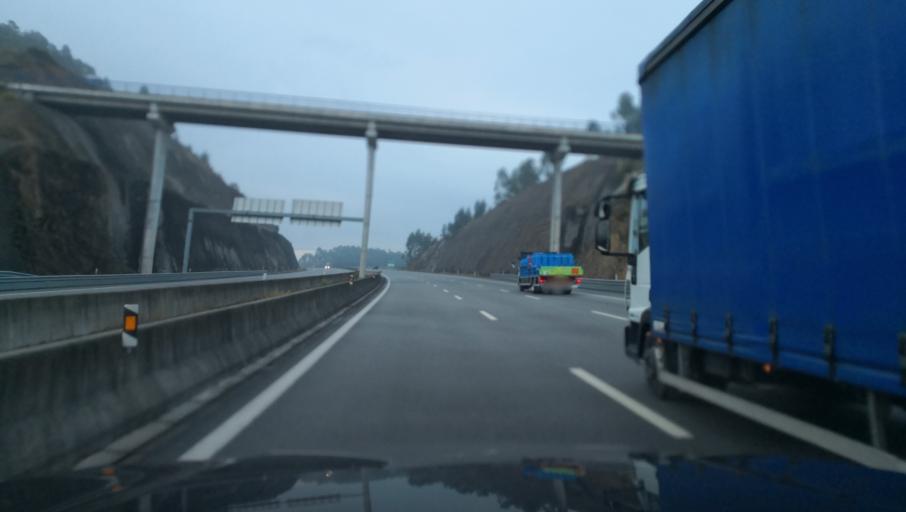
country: PT
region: Porto
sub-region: Paredes
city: Recarei
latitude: 41.1262
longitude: -8.4323
